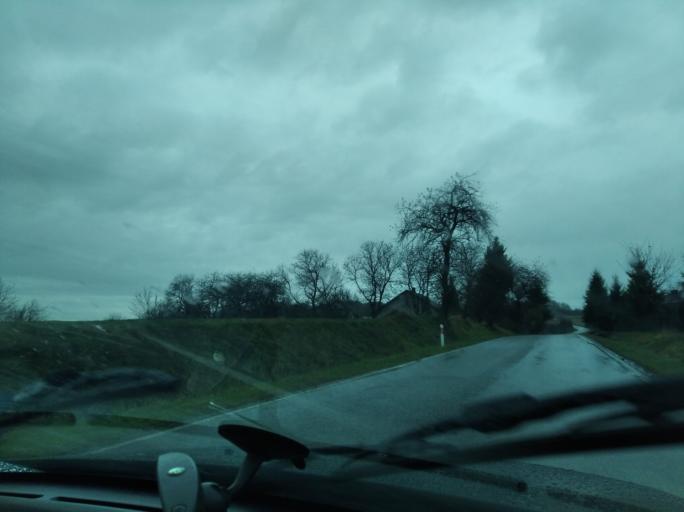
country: PL
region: Subcarpathian Voivodeship
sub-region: Powiat lancucki
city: Handzlowka
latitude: 49.9792
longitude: 22.1921
